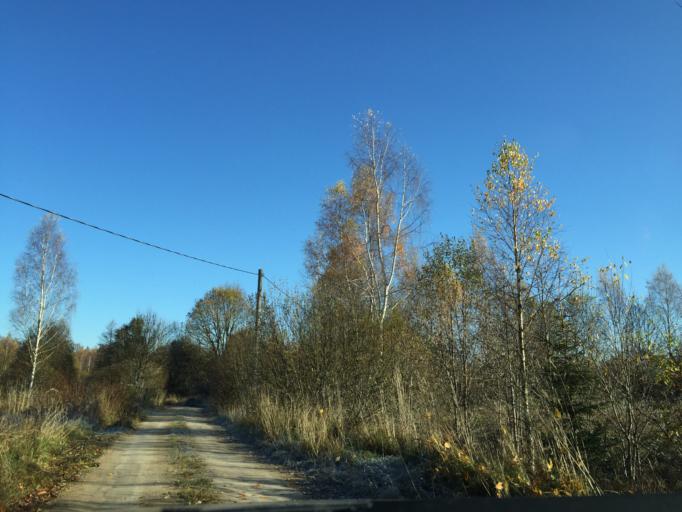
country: LV
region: Aizkraukles Rajons
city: Aizkraukle
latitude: 56.7083
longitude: 25.2988
